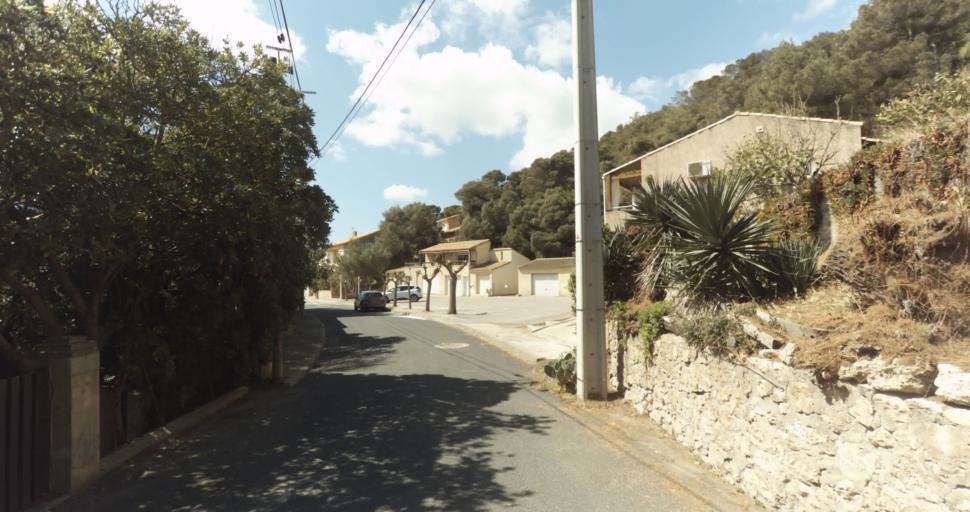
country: FR
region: Languedoc-Roussillon
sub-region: Departement de l'Aude
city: Leucate
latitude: 42.9066
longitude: 3.0559
